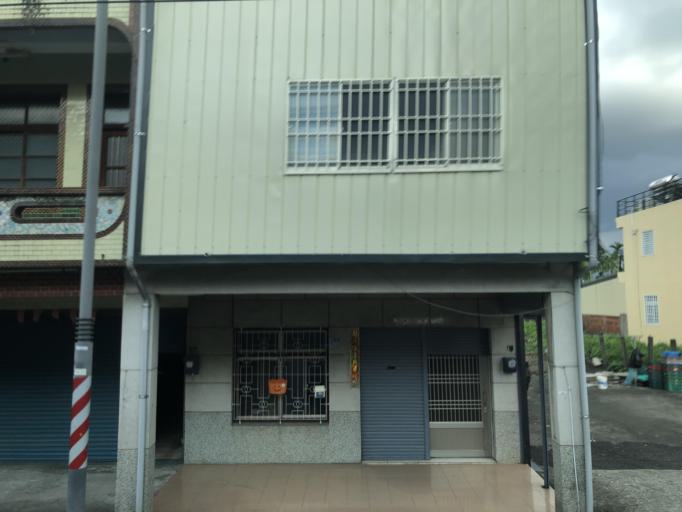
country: TW
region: Taiwan
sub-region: Pingtung
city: Pingtung
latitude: 22.8734
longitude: 120.5364
